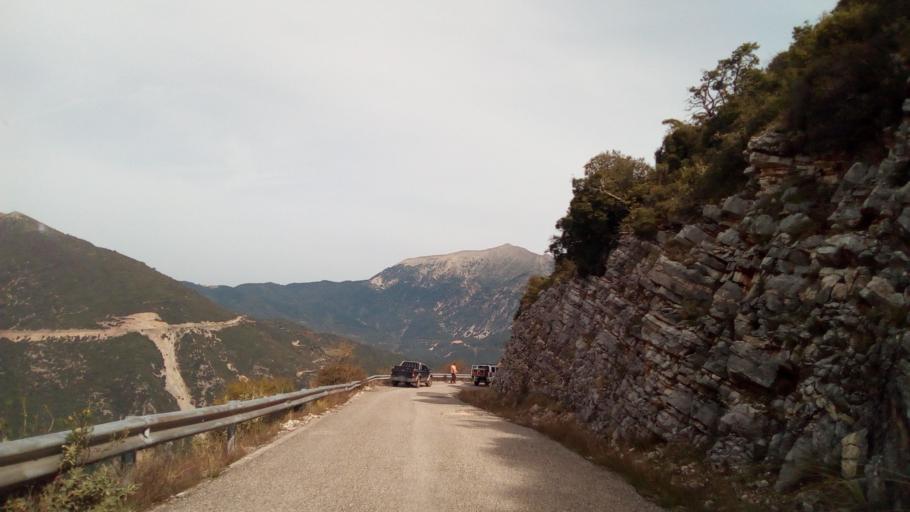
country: GR
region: West Greece
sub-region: Nomos Aitolias kai Akarnanias
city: Thermo
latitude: 38.5721
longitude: 21.8198
